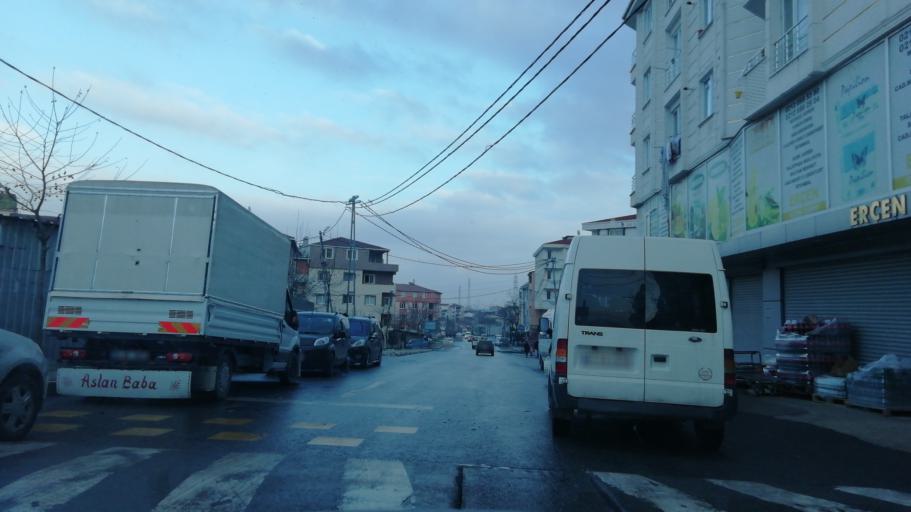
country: TR
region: Istanbul
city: Esenyurt
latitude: 41.0293
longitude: 28.6976
